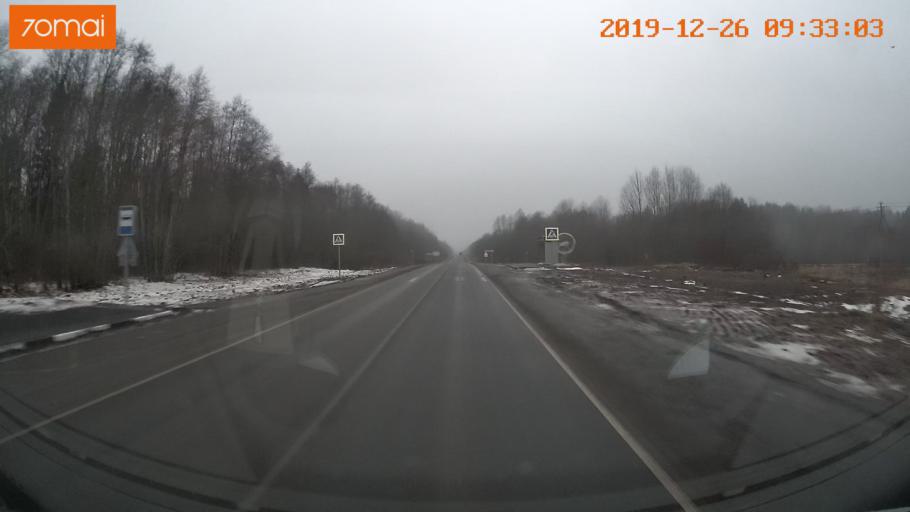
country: RU
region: Vologda
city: Gryazovets
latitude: 59.0853
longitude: 40.1067
